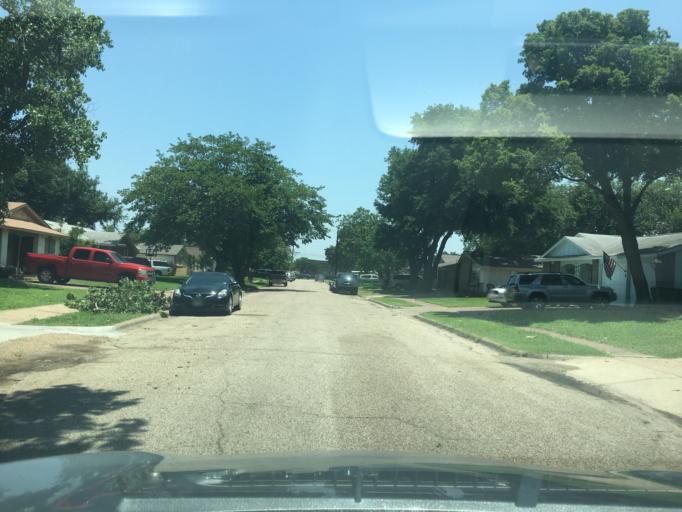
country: US
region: Texas
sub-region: Dallas County
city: Garland
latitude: 32.9149
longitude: -96.6849
